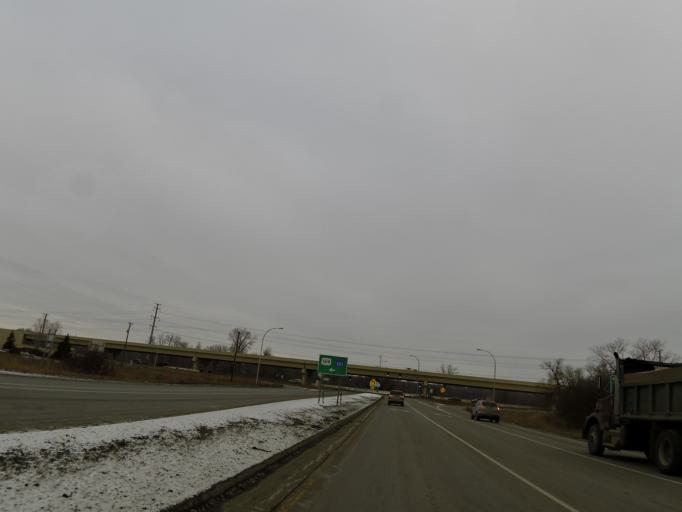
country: US
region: Minnesota
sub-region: Scott County
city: Savage
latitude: 44.7775
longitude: -93.3782
